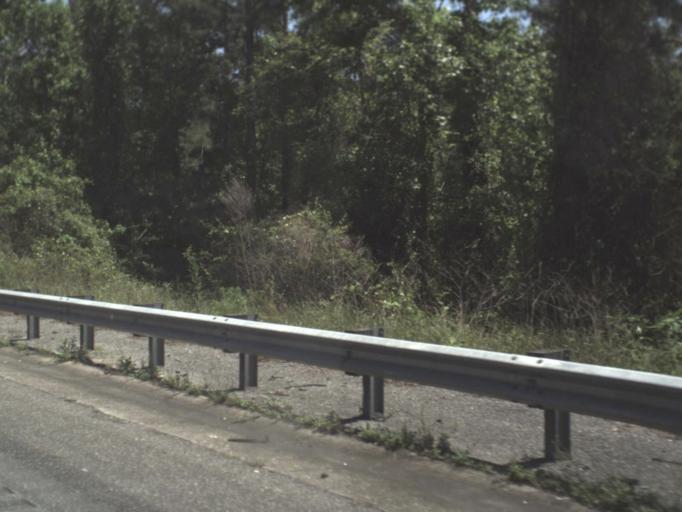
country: US
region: Florida
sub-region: Jefferson County
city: Monticello
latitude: 30.4729
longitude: -83.8541
